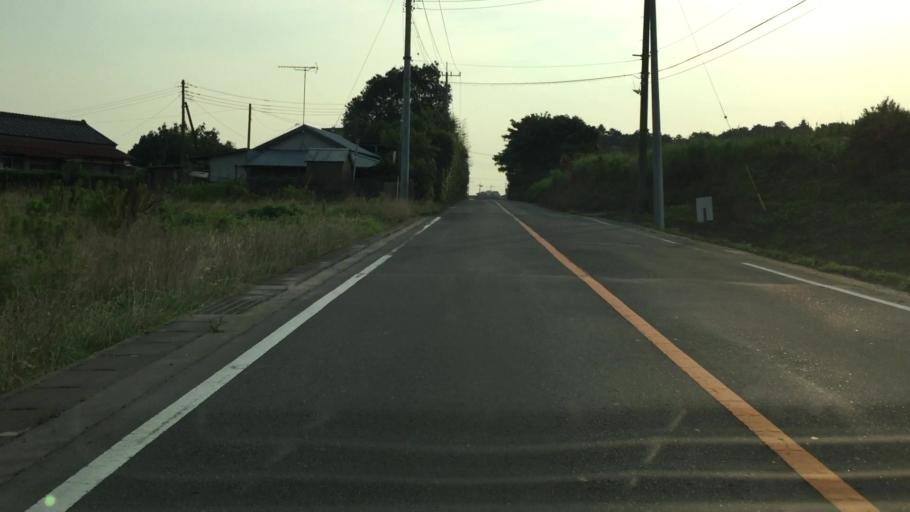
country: JP
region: Tochigi
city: Fujioka
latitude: 36.2611
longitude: 139.6277
